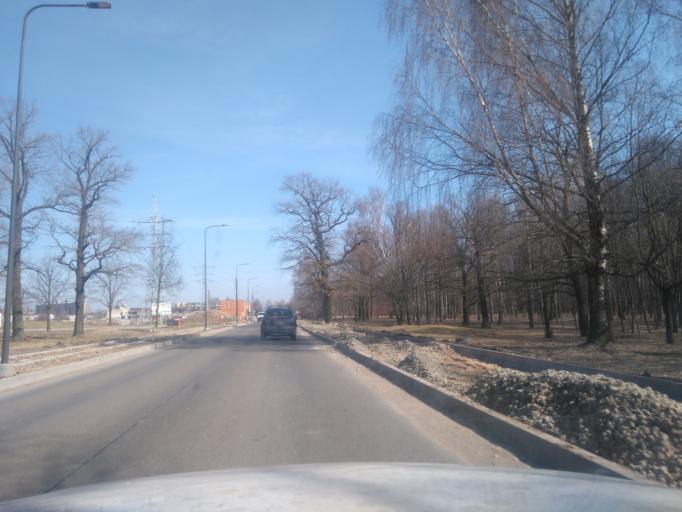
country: LT
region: Kauno apskritis
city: Dainava (Kaunas)
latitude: 54.8821
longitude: 23.9489
